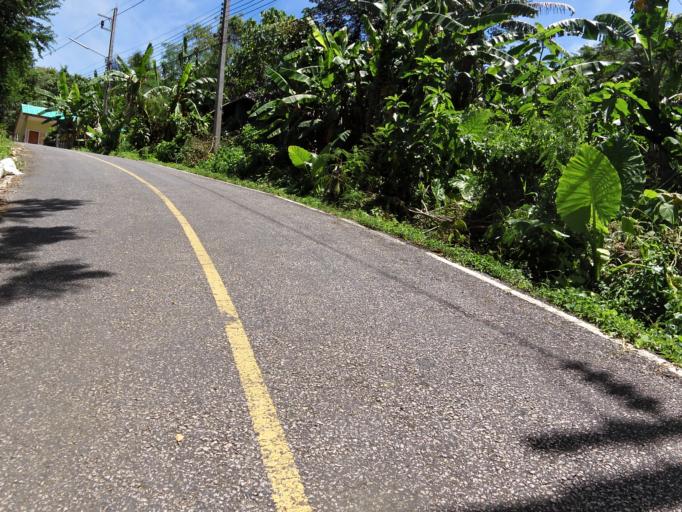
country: TH
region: Phuket
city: Ban Karon
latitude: 7.8478
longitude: 98.3079
